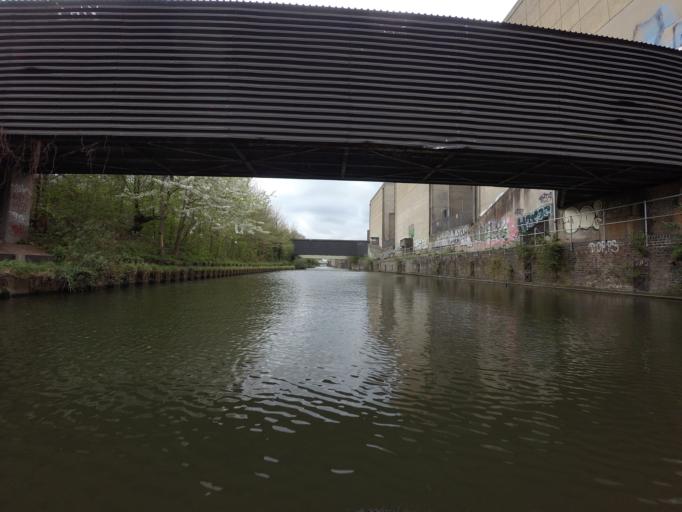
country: GB
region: England
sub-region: Greater London
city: Acton
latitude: 51.5331
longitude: -0.2560
